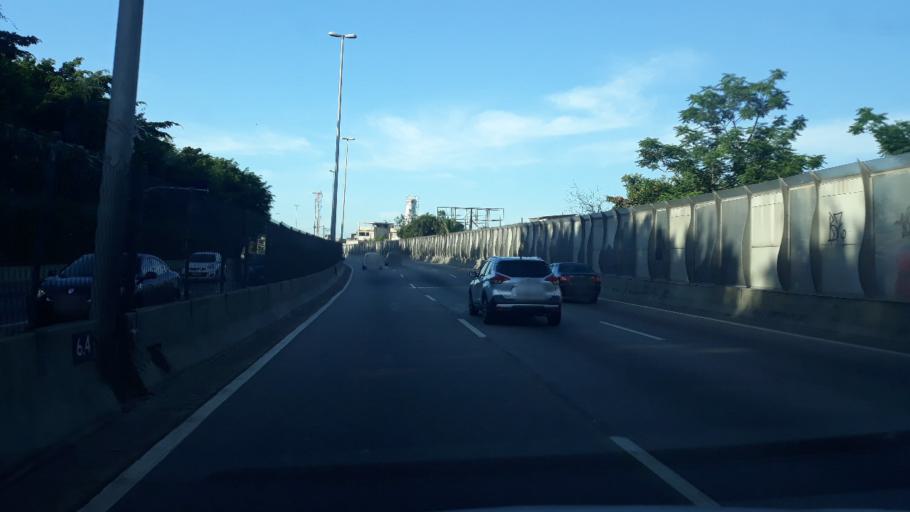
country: BR
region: Rio de Janeiro
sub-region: Sao Joao De Meriti
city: Sao Joao de Meriti
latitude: -22.9485
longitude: -43.3558
